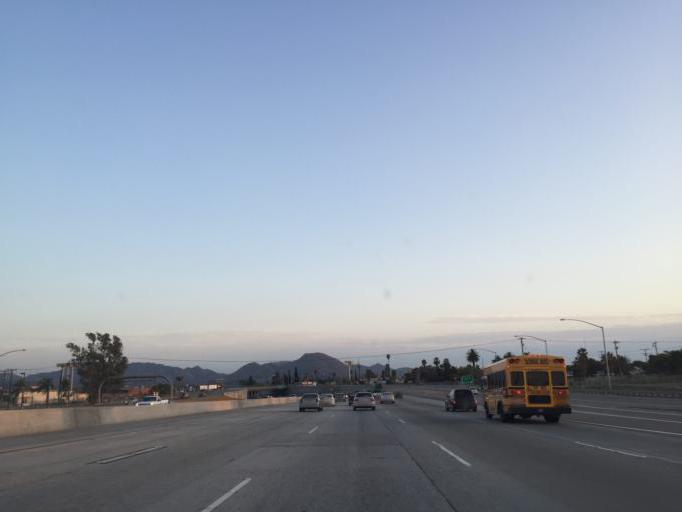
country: US
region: California
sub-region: San Bernardino County
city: Colton
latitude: 34.0898
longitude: -117.3021
